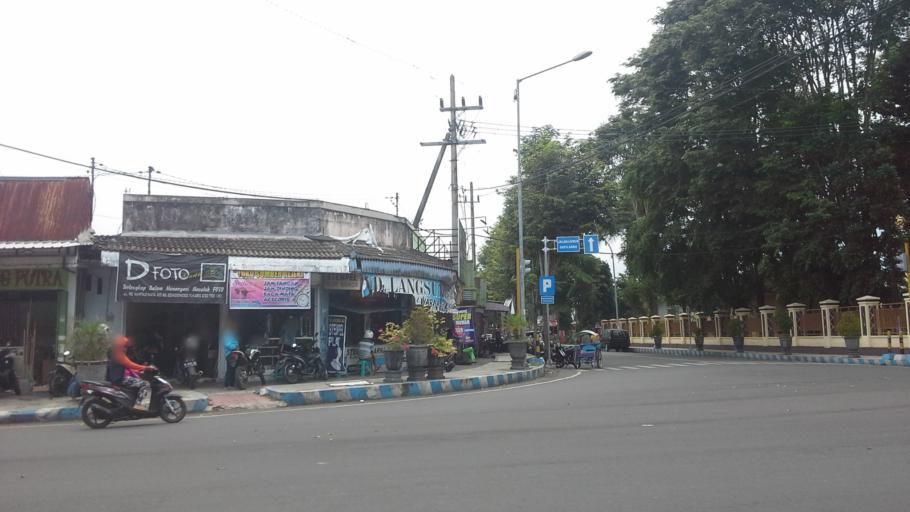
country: ID
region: East Java
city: Bondowoso
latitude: -7.9144
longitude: 113.8233
